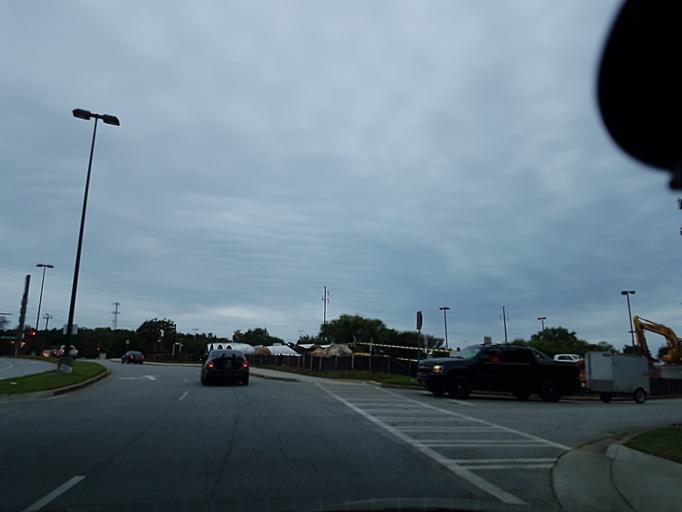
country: US
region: Georgia
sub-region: DeKalb County
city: Tucker
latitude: 33.8327
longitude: -84.1970
